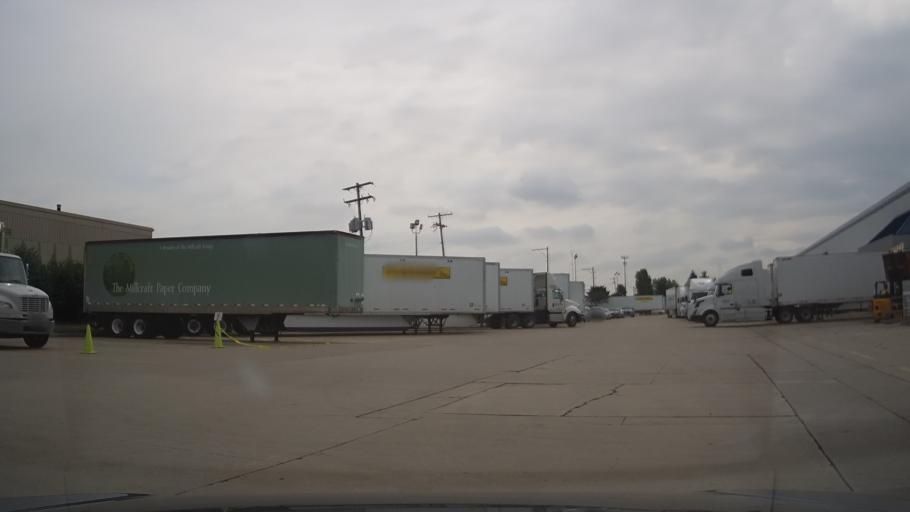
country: US
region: Ohio
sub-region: Franklin County
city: Lincoln Village
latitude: 39.9601
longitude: -83.1176
